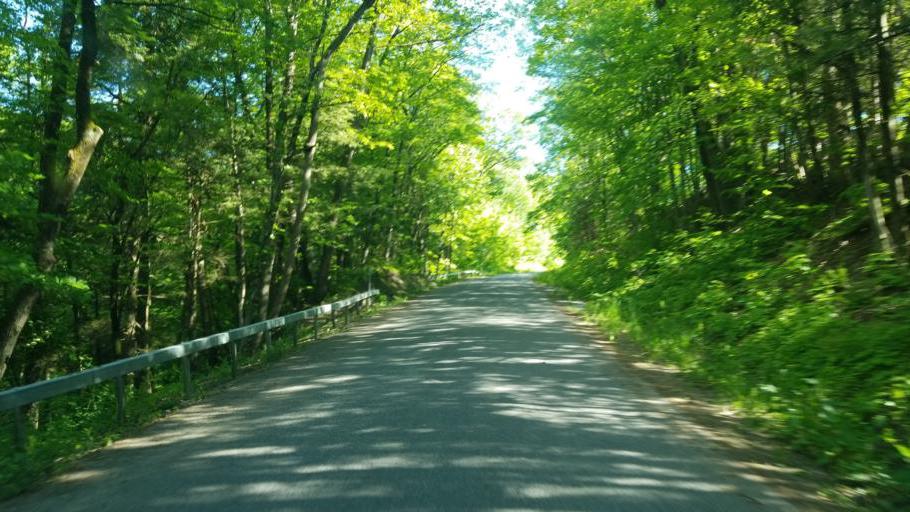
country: US
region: New York
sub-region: Herkimer County
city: Little Falls
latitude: 43.0002
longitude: -74.7789
